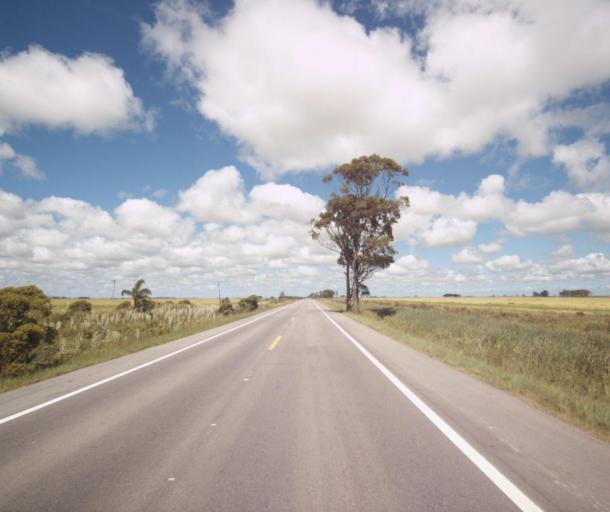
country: BR
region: Rio Grande do Sul
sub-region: Rio Grande
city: Rio Grande
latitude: -32.1572
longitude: -52.3982
